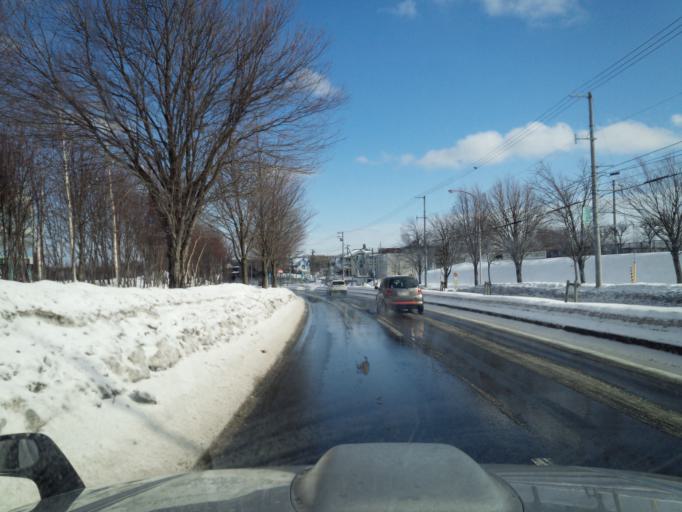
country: JP
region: Hokkaido
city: Kitahiroshima
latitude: 42.9974
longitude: 141.4603
